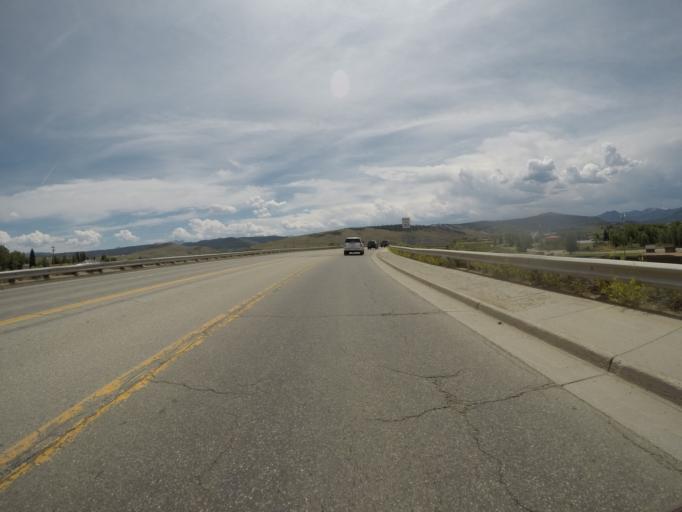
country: US
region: Colorado
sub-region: Grand County
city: Granby
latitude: 40.0843
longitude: -105.9310
